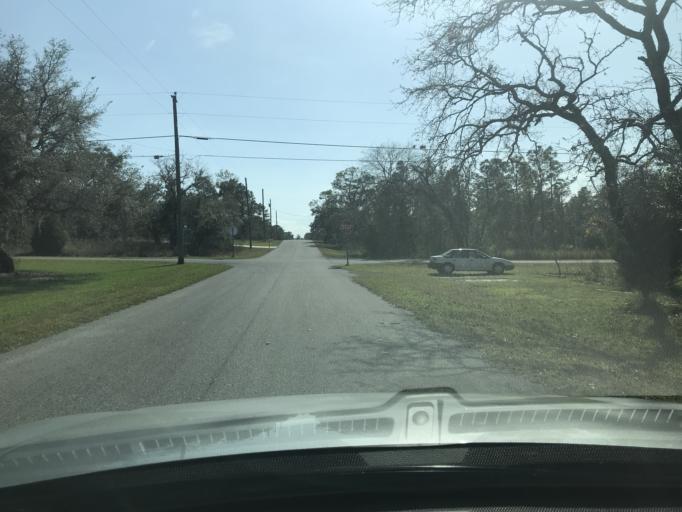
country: US
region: Florida
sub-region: Hernando County
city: North Weeki Wachee
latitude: 28.5514
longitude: -82.5490
